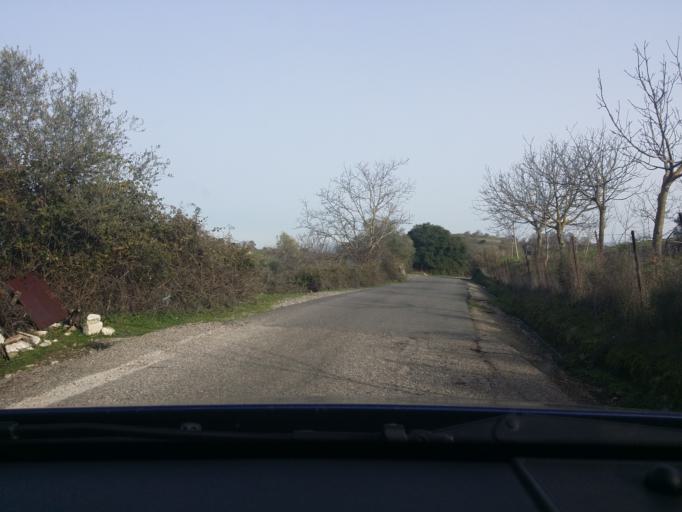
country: GR
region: West Greece
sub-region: Nomos Aitolias kai Akarnanias
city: Katouna
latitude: 38.8228
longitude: 21.0785
